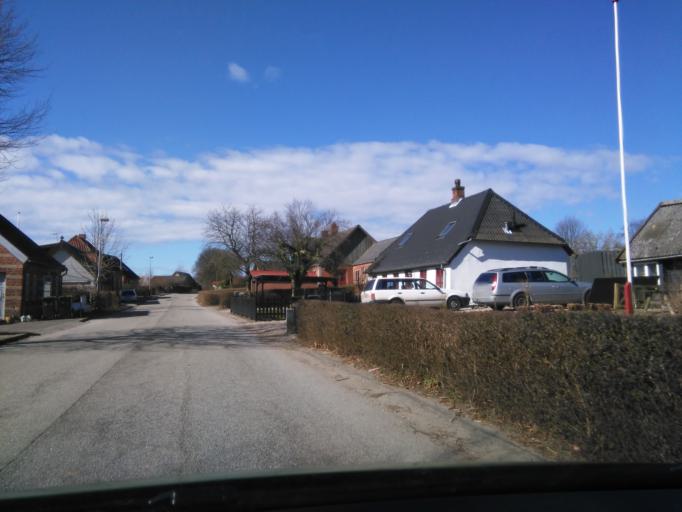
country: DK
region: Central Jutland
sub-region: Skanderborg Kommune
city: Skanderborg
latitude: 55.9619
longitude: 9.9837
